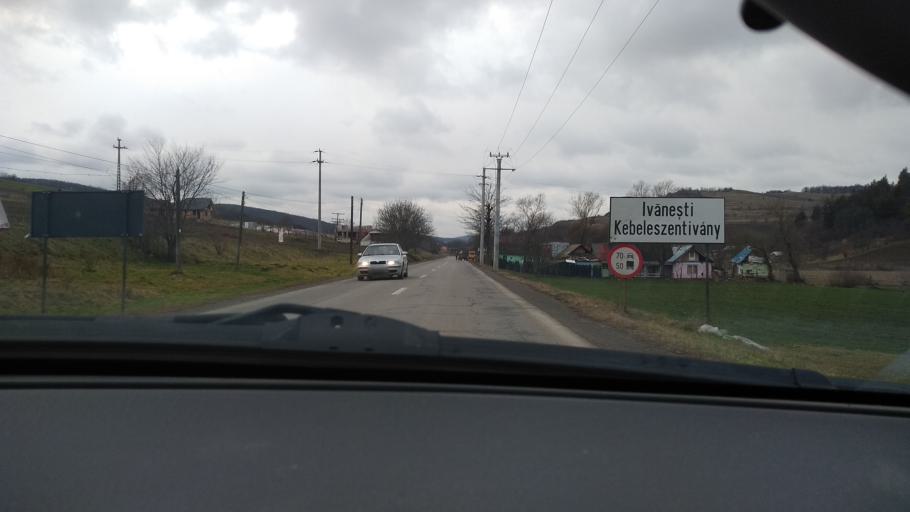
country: RO
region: Mures
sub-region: Comuna Livezeni
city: Livezeni
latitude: 46.5417
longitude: 24.6910
